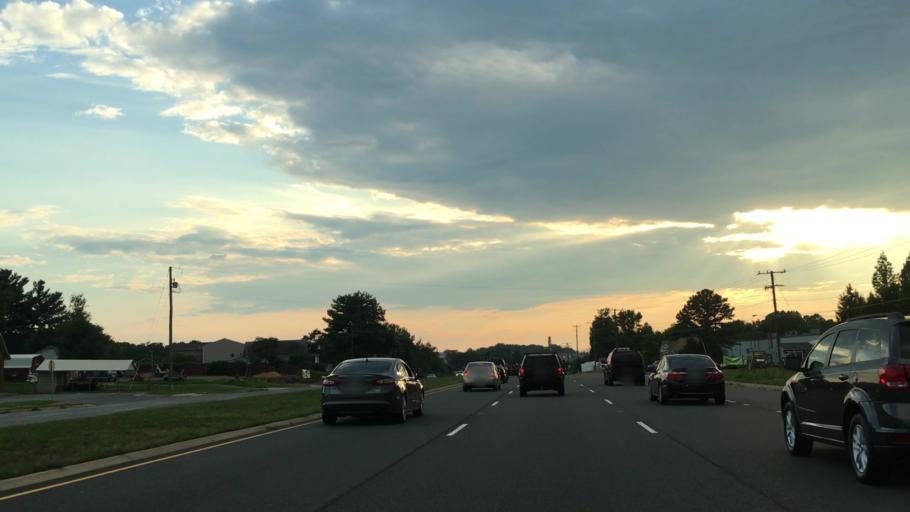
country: US
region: Virginia
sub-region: Stafford County
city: Falmouth
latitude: 38.2905
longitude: -77.5546
